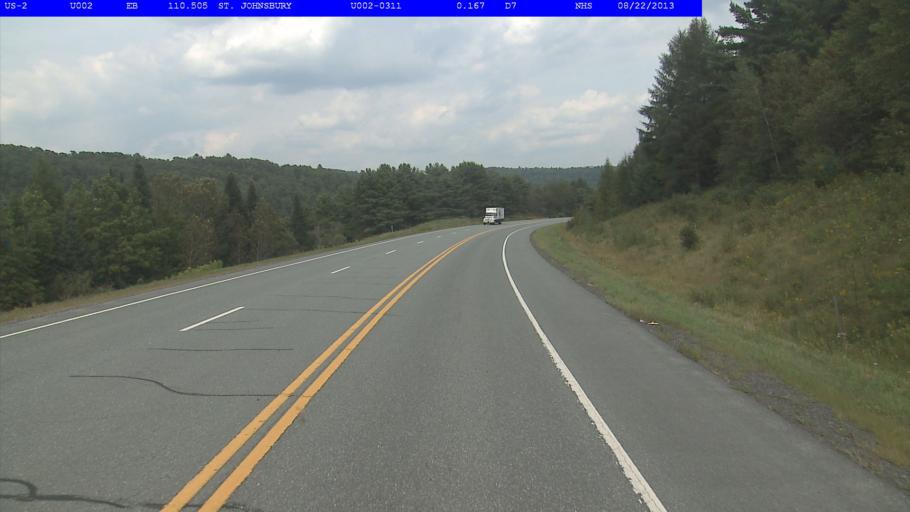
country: US
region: Vermont
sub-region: Caledonia County
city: St Johnsbury
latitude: 44.4443
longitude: -72.0578
